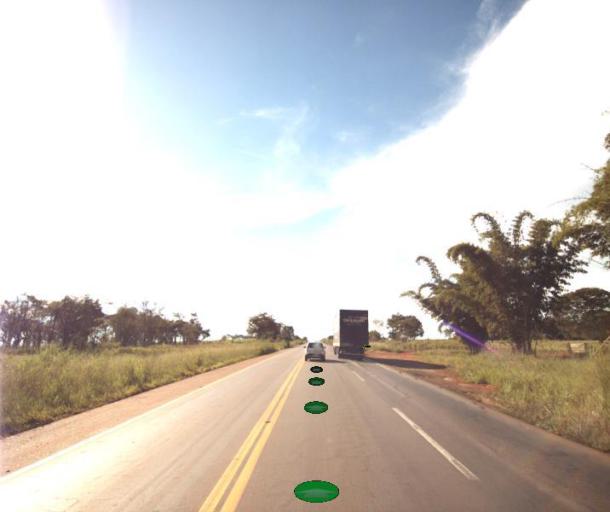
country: BR
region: Goias
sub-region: Rialma
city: Rialma
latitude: -15.3808
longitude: -49.5538
